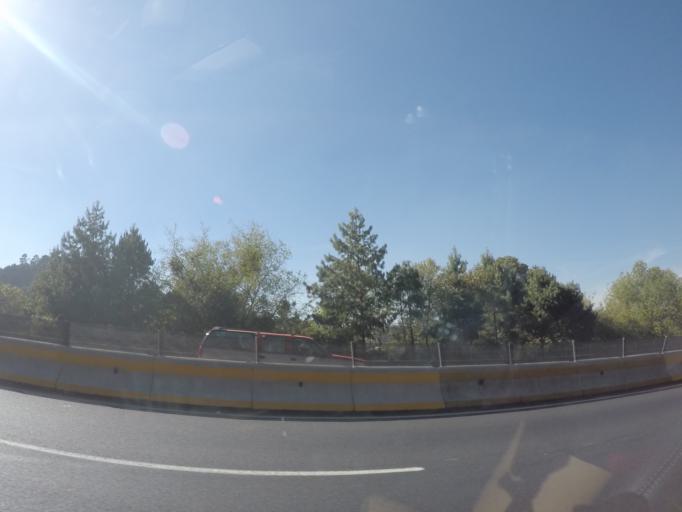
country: MX
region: Mexico City
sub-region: Cuajimalpa de Morelos
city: San Lorenzo Acopilco
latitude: 19.3228
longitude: -99.3191
